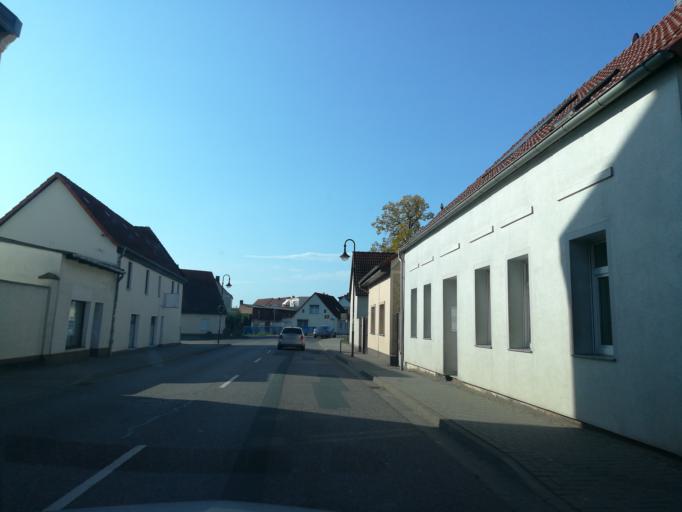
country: DE
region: Saxony-Anhalt
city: Gommern
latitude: 52.0727
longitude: 11.8237
